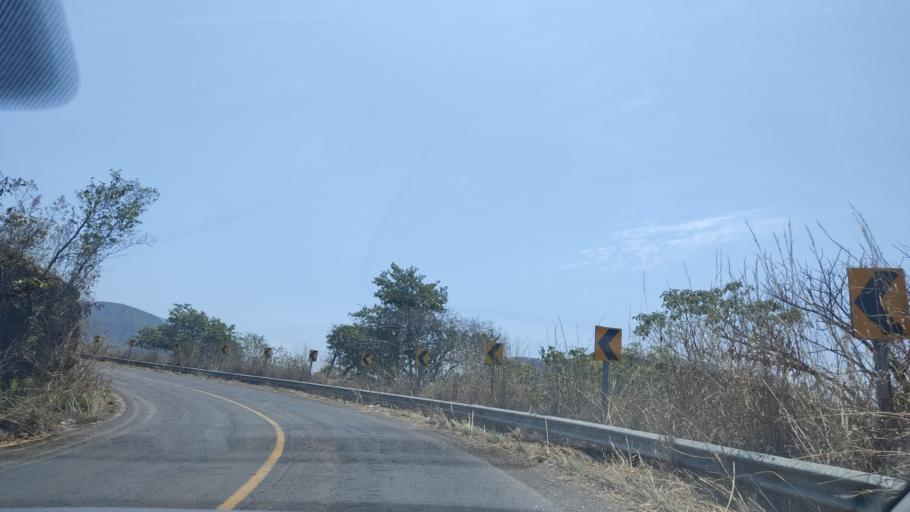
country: MX
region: Nayarit
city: Puga
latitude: 21.5751
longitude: -104.7610
